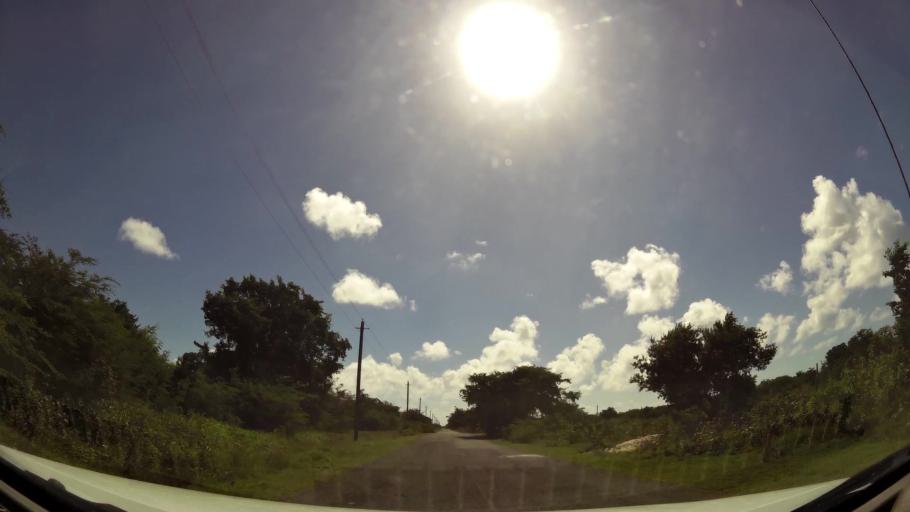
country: AG
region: Barbuda
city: Codrington
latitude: 17.6104
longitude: -61.8286
